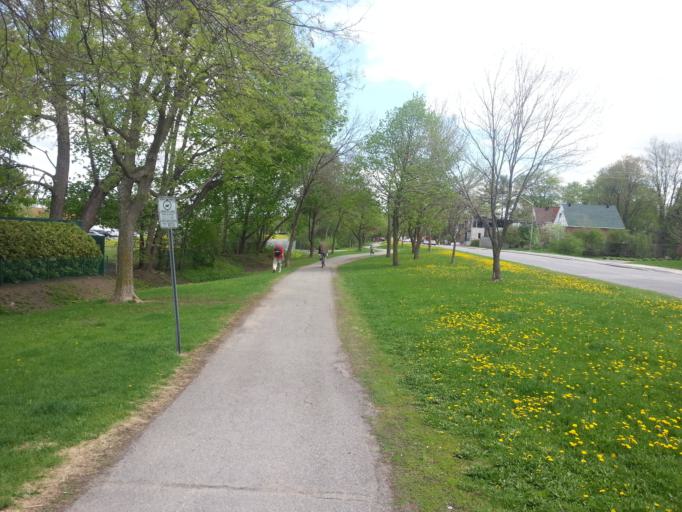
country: CA
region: Ontario
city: Ottawa
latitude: 45.3925
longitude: -75.7489
